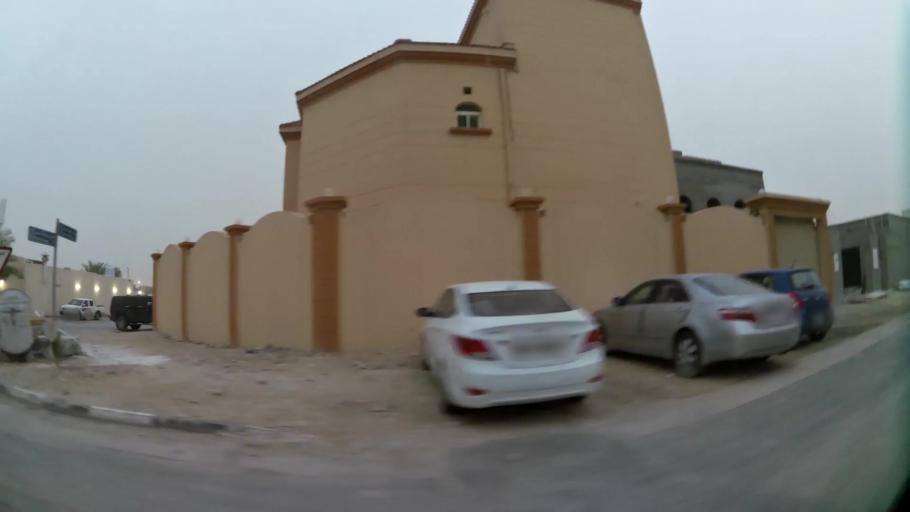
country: QA
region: Baladiyat ad Dawhah
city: Doha
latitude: 25.2286
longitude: 51.4933
